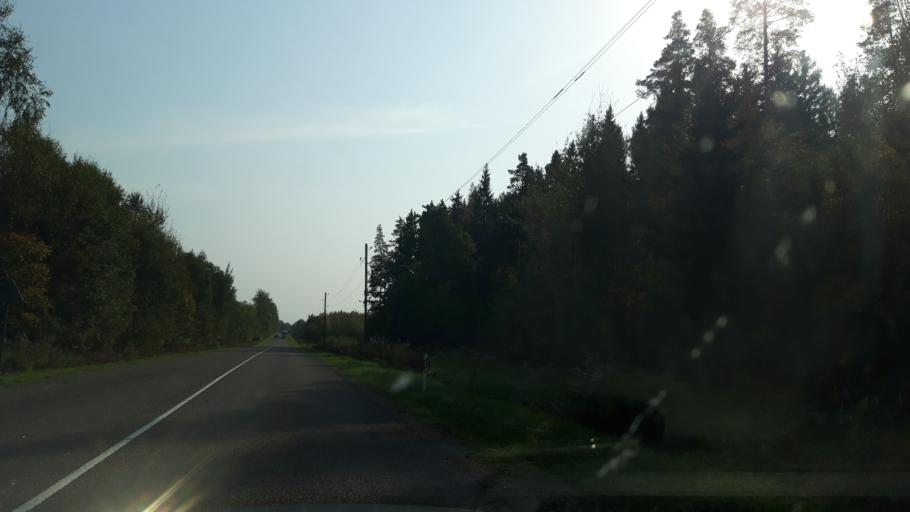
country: LV
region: Burtnieki
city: Matisi
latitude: 57.6371
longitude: 25.2544
